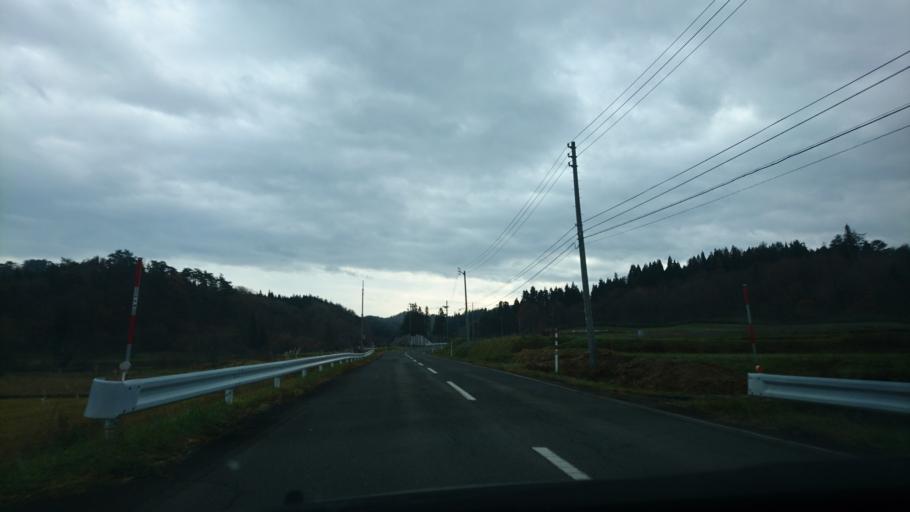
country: JP
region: Iwate
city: Ichinoseki
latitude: 38.9359
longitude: 140.9205
